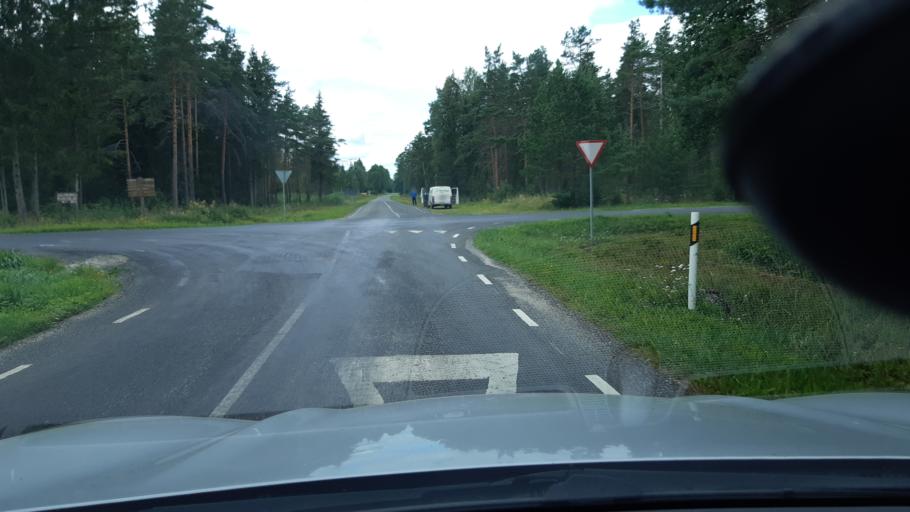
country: EE
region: Raplamaa
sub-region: Rapla vald
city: Rapla
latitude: 58.8863
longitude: 24.7258
